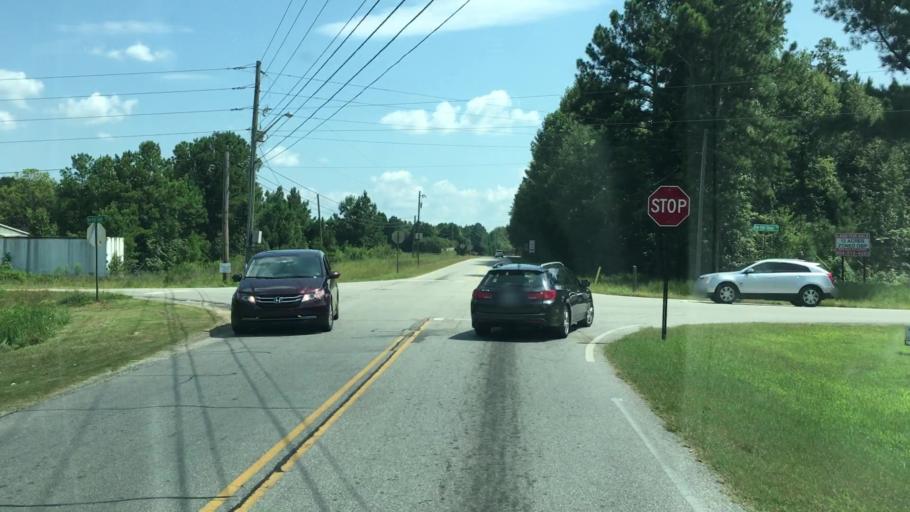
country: US
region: Georgia
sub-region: Oconee County
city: Watkinsville
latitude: 33.8433
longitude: -83.4479
